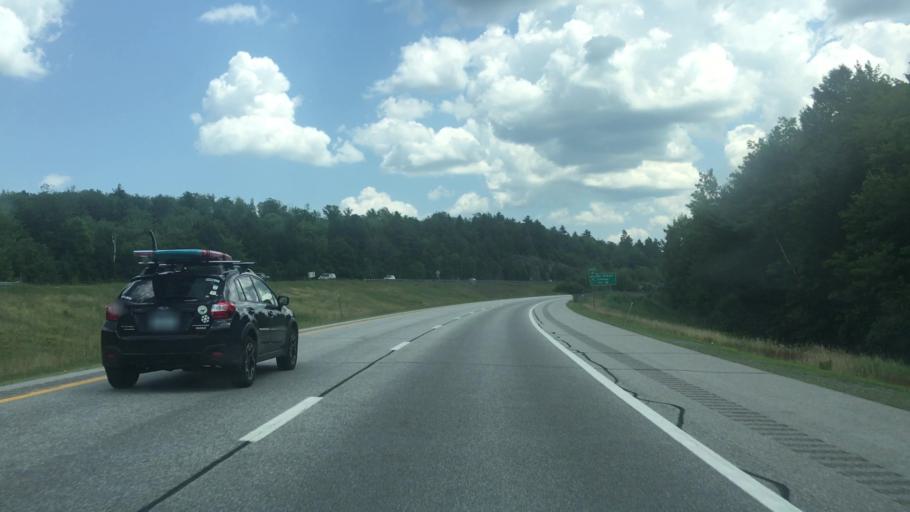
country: US
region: New Hampshire
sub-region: Sullivan County
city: Springfield
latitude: 43.4366
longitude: -72.0464
